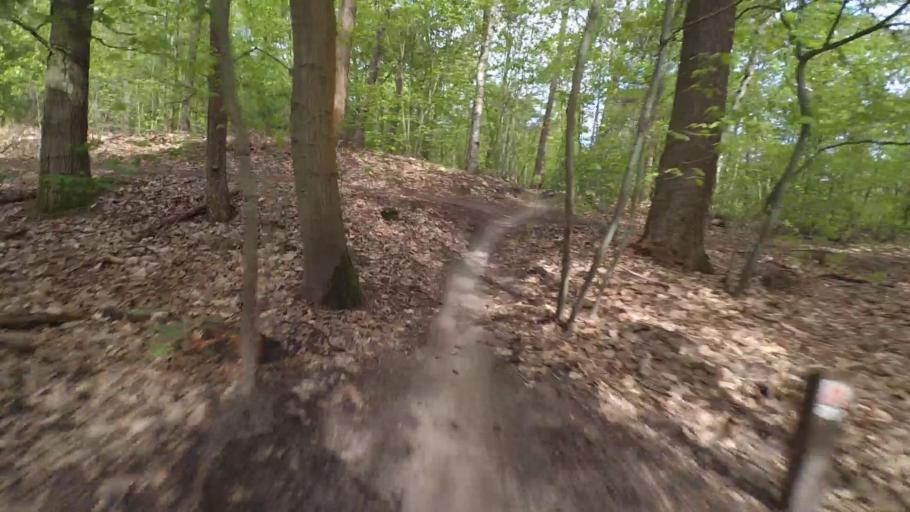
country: NL
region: Utrecht
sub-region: Gemeente Utrechtse Heuvelrug
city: Driebergen-Rijsenburg
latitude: 52.0848
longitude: 5.2731
